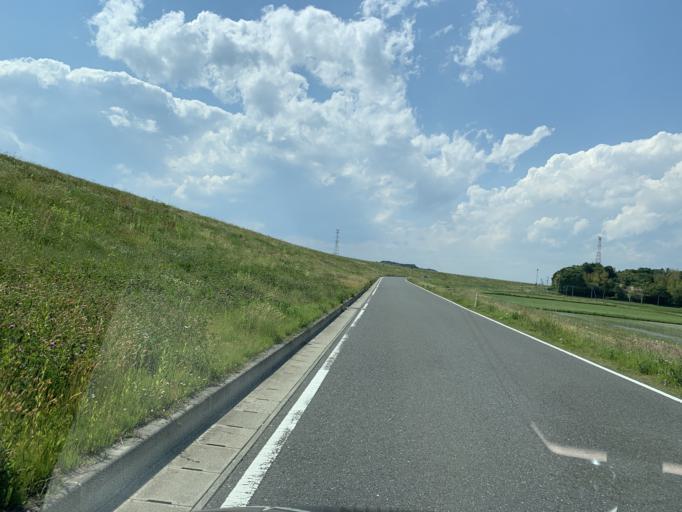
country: JP
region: Miyagi
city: Matsushima
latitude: 38.4233
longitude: 141.1296
